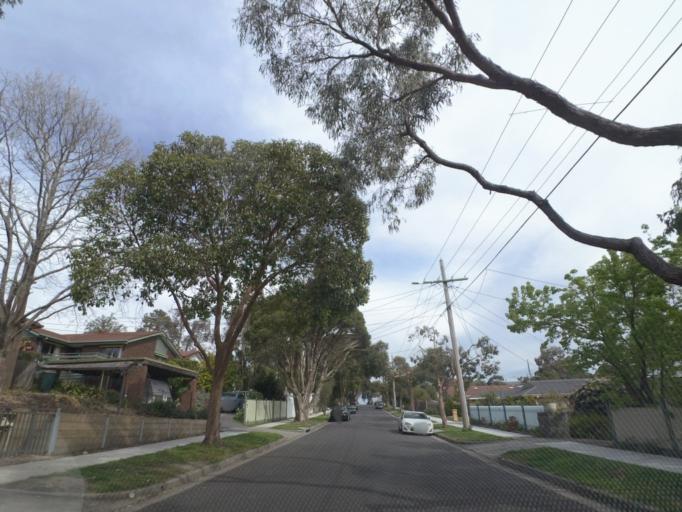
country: AU
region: Victoria
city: Mitcham
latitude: -37.8096
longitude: 145.2038
